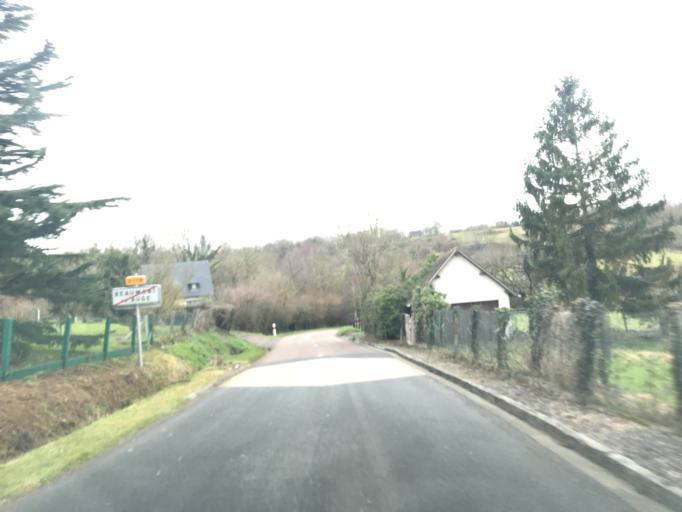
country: FR
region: Lower Normandy
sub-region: Departement du Calvados
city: Touques
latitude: 49.2782
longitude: 0.1072
